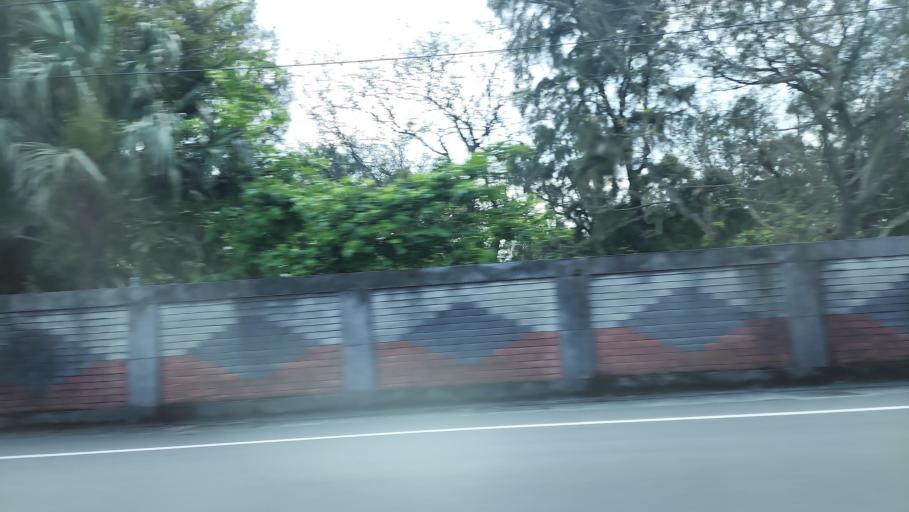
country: TW
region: Taiwan
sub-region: Keelung
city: Keelung
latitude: 25.2261
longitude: 121.6436
